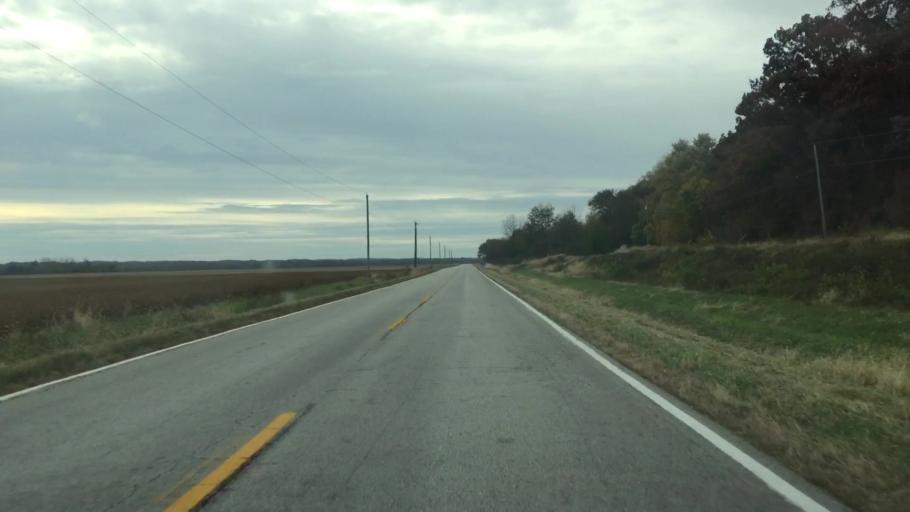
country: US
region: Missouri
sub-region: Gasconade County
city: Hermann
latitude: 38.7083
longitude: -91.5446
